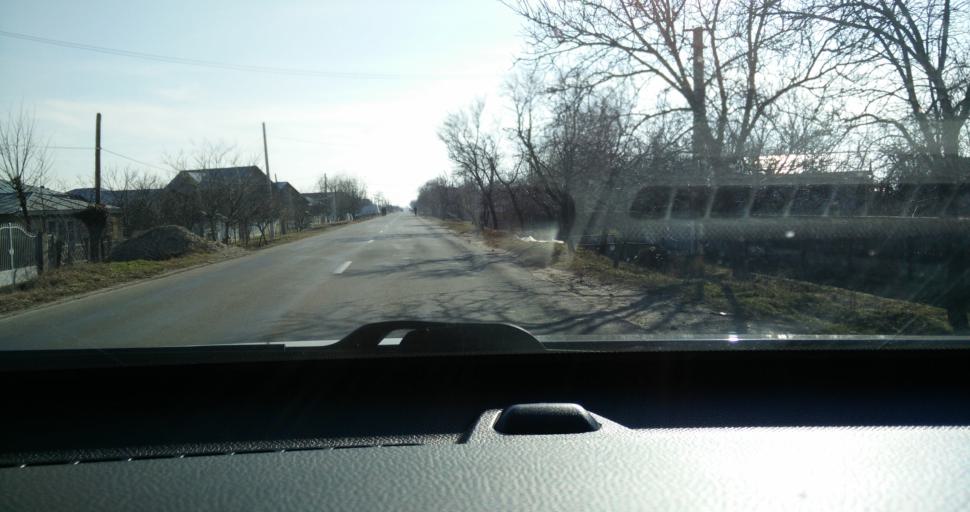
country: RO
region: Vrancea
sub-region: Comuna Nanesti
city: Nanesti
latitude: 45.5313
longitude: 27.4974
